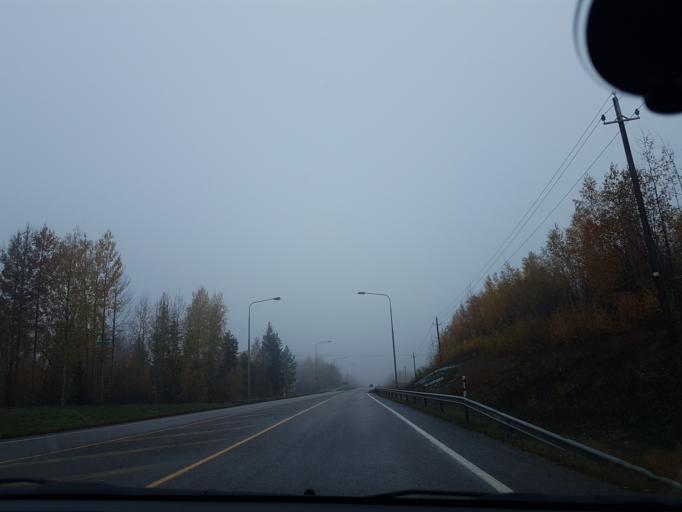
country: FI
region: Uusimaa
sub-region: Helsinki
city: Jaervenpaeae
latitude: 60.4523
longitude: 25.1361
